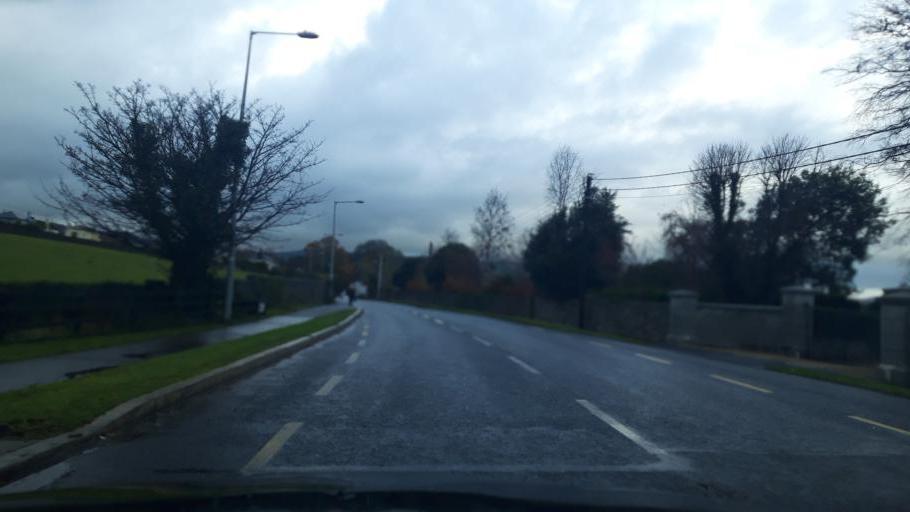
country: IE
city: Newtownmountkennedy
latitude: 53.0866
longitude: -6.1064
